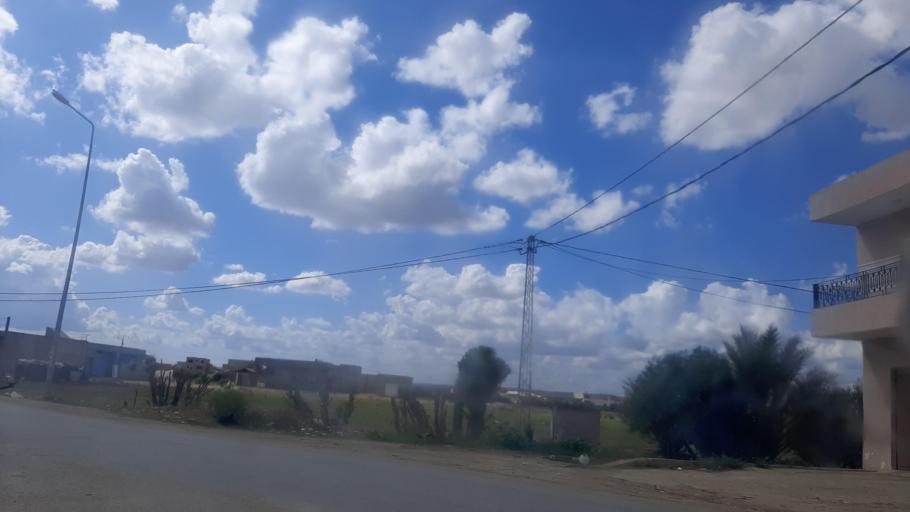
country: TN
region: Nabul
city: Korba
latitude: 36.5894
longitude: 10.8558
